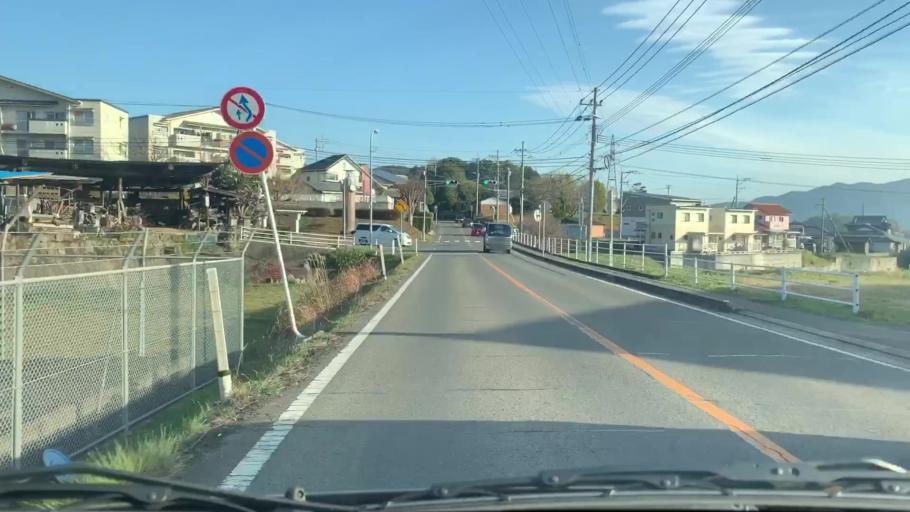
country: JP
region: Saga Prefecture
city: Takeocho-takeo
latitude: 33.2082
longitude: 130.0274
